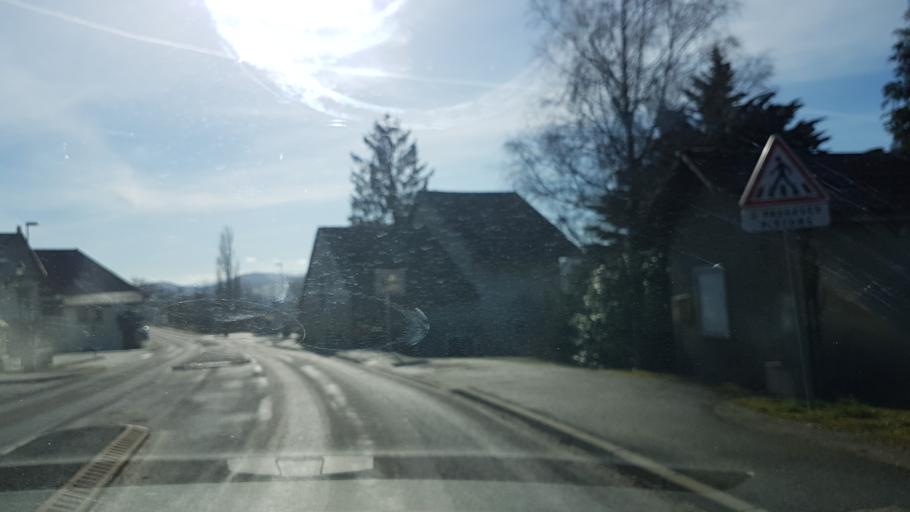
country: FR
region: Rhone-Alpes
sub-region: Departement de la Haute-Savoie
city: Frangy
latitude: 46.0430
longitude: 5.8855
